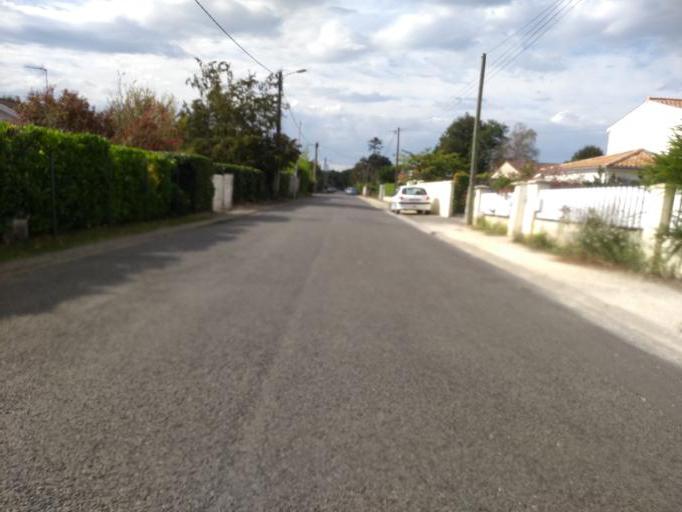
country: FR
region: Aquitaine
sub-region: Departement de la Gironde
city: Saint-Aubin-de-Medoc
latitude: 44.7716
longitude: -0.6964
